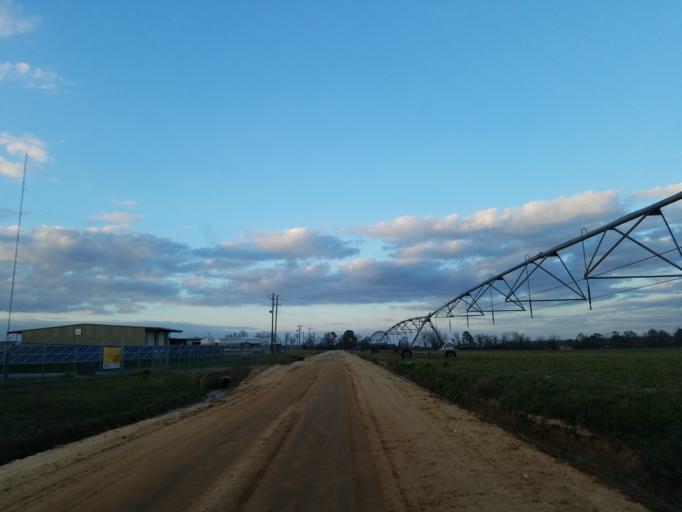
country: US
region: Georgia
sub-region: Dooly County
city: Vienna
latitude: 32.0888
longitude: -83.7521
